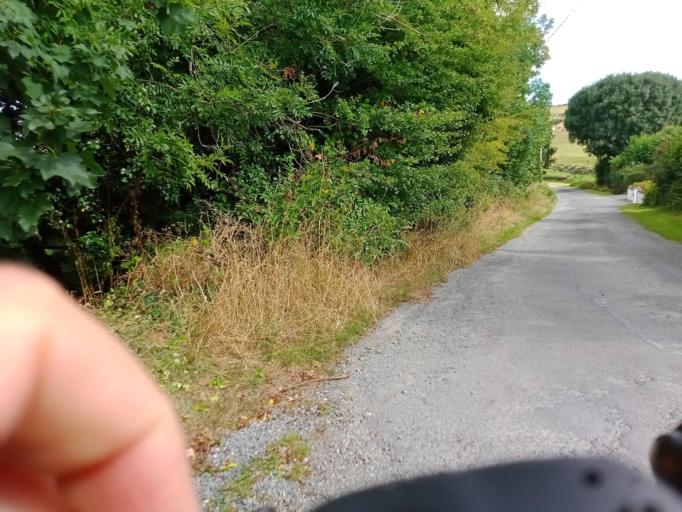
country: IE
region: Munster
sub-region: Waterford
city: Dungarvan
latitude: 52.1131
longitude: -7.5071
